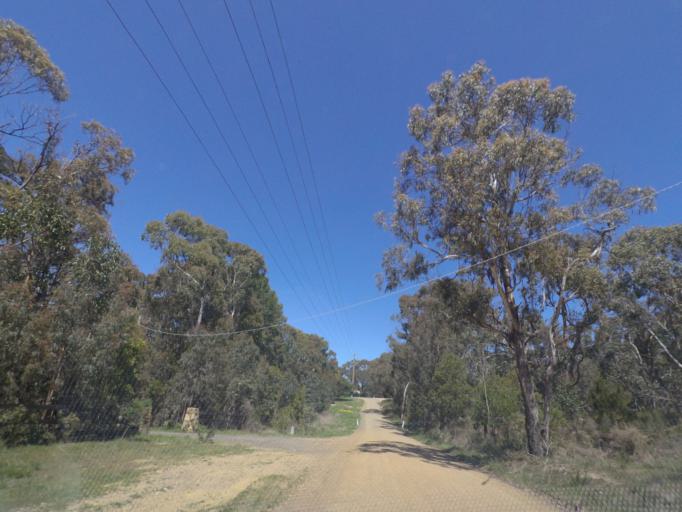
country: AU
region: Victoria
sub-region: Hume
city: Sunbury
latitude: -37.4104
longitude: 144.5614
